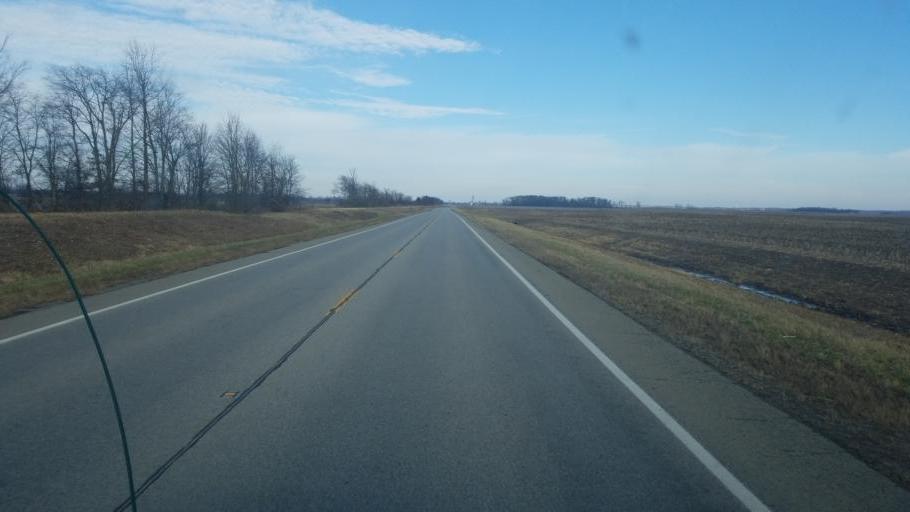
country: US
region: Illinois
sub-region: White County
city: Carmi
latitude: 38.1235
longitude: -88.1074
